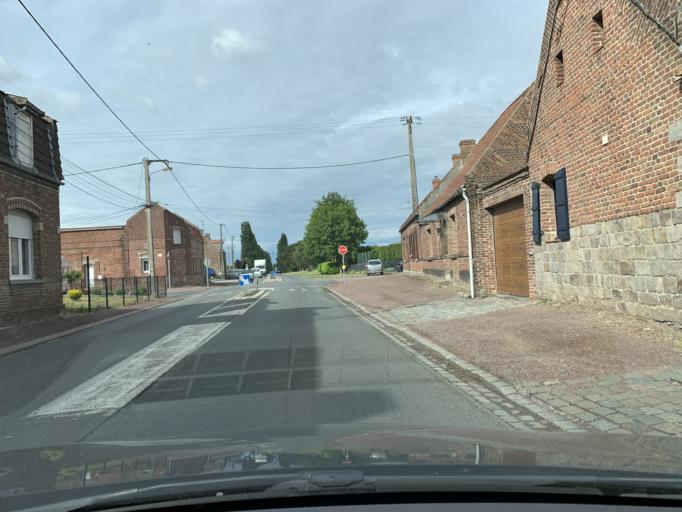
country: FR
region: Nord-Pas-de-Calais
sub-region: Departement du Nord
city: Lewarde
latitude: 50.3287
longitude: 3.1513
